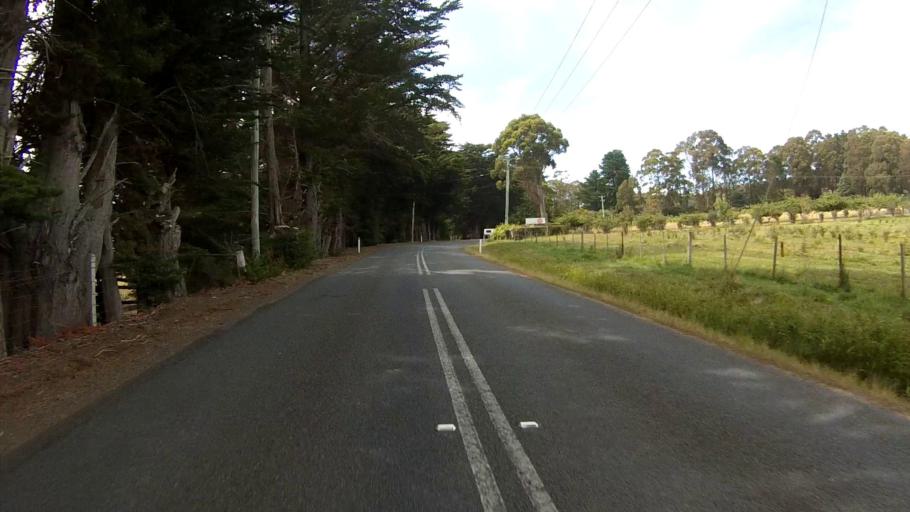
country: AU
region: Tasmania
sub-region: Kingborough
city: Kettering
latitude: -43.1882
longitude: 147.2444
